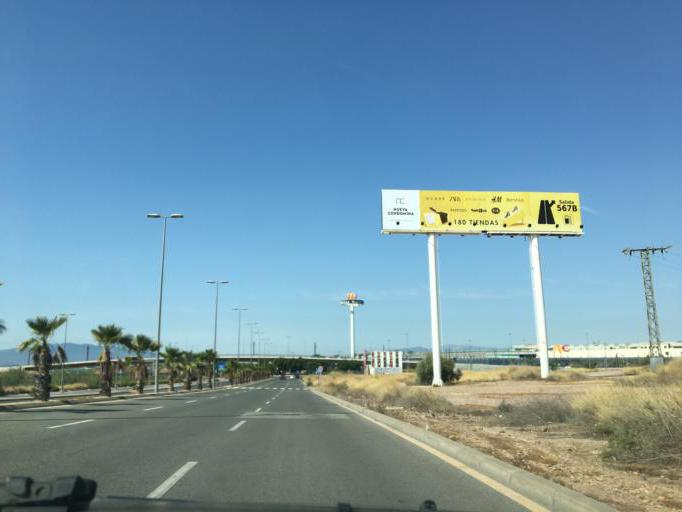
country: ES
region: Murcia
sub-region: Murcia
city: Murcia
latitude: 38.0403
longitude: -1.1423
